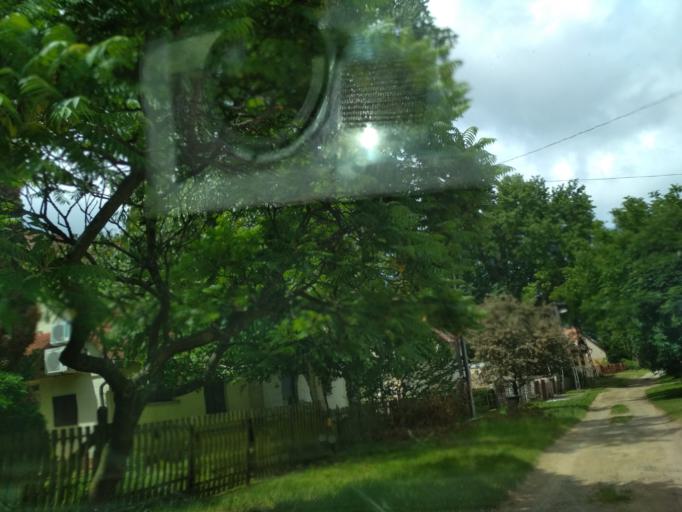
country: HU
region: Jasz-Nagykun-Szolnok
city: Tiszafured
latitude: 47.6168
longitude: 20.7319
